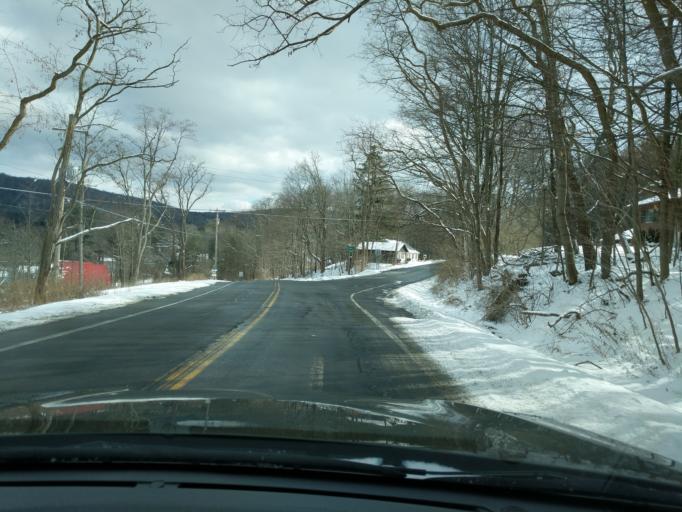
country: US
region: New York
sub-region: Tompkins County
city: Northeast Ithaca
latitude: 42.4260
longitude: -76.3906
